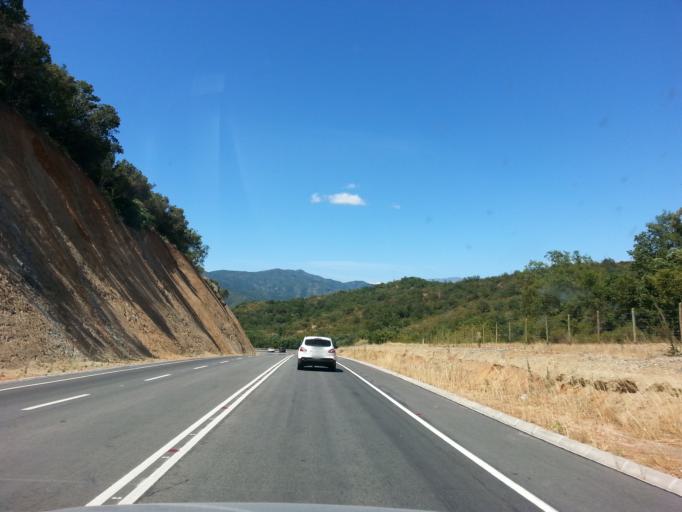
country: CL
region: Valparaiso
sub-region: Provincia de Marga Marga
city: Villa Alemana
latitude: -33.1726
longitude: -71.3548
